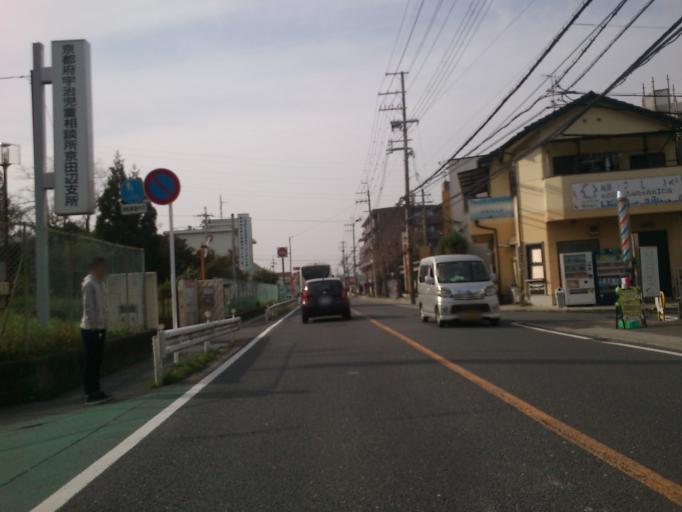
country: JP
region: Kyoto
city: Tanabe
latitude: 34.8117
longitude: 135.7727
